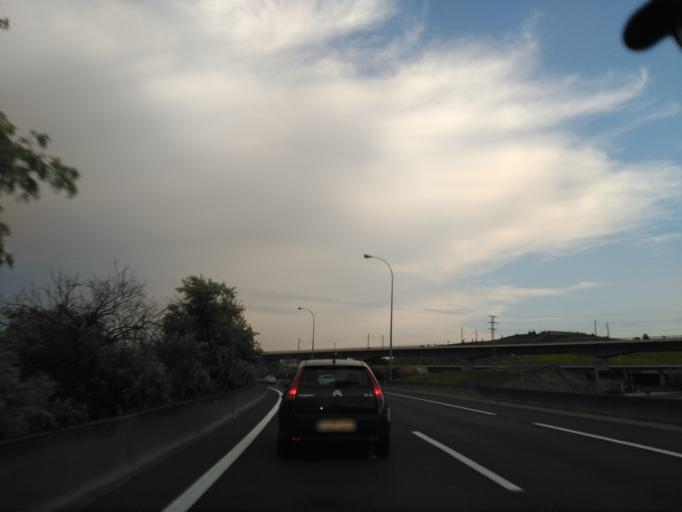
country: ES
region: Madrid
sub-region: Provincia de Madrid
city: Villaverde
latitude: 40.3598
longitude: -3.6779
